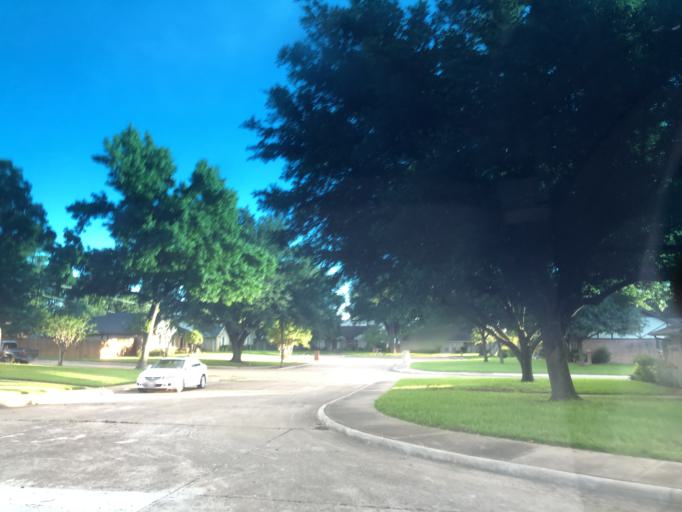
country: US
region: Texas
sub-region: Dallas County
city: Grand Prairie
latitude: 32.7813
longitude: -97.0367
